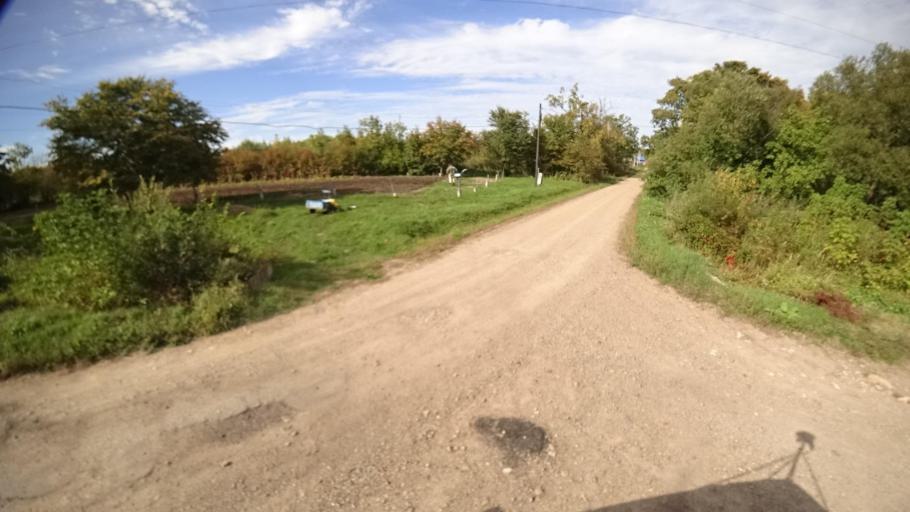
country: RU
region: Primorskiy
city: Dostoyevka
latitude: 44.2968
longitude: 133.4624
